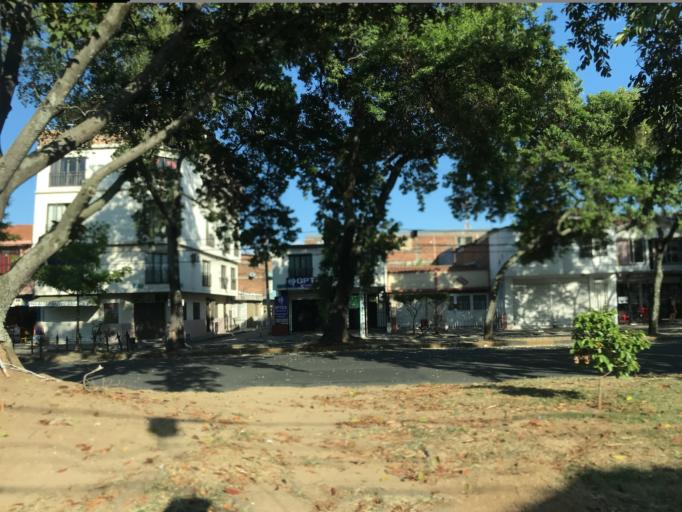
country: CO
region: Valle del Cauca
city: Cali
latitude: 3.4371
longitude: -76.5280
